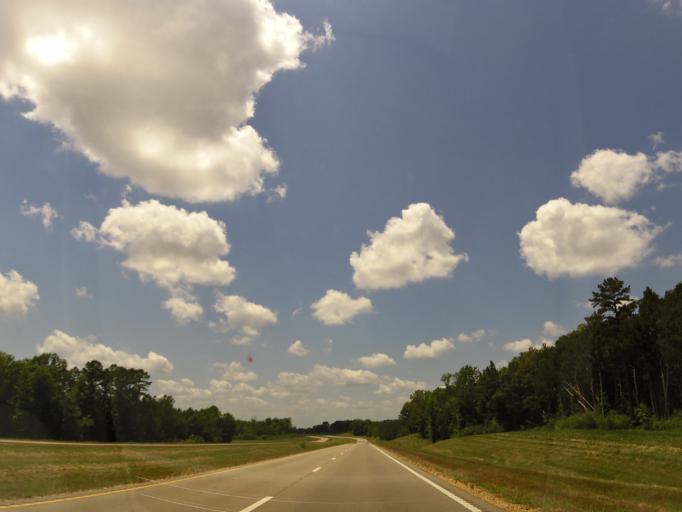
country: US
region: Mississippi
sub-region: Lee County
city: Verona
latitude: 34.2194
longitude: -88.8268
